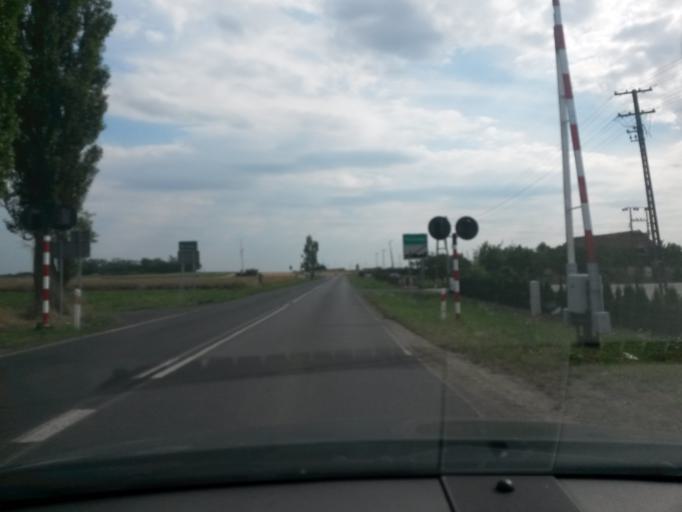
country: PL
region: Greater Poland Voivodeship
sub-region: Powiat gostynski
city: Krobia
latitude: 51.7591
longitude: 16.9671
